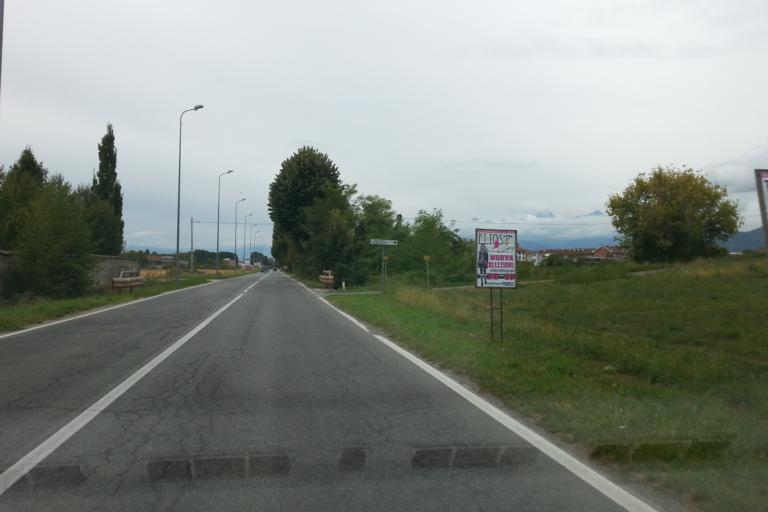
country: IT
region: Piedmont
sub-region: Provincia di Torino
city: Riva
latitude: 44.8974
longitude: 7.3567
